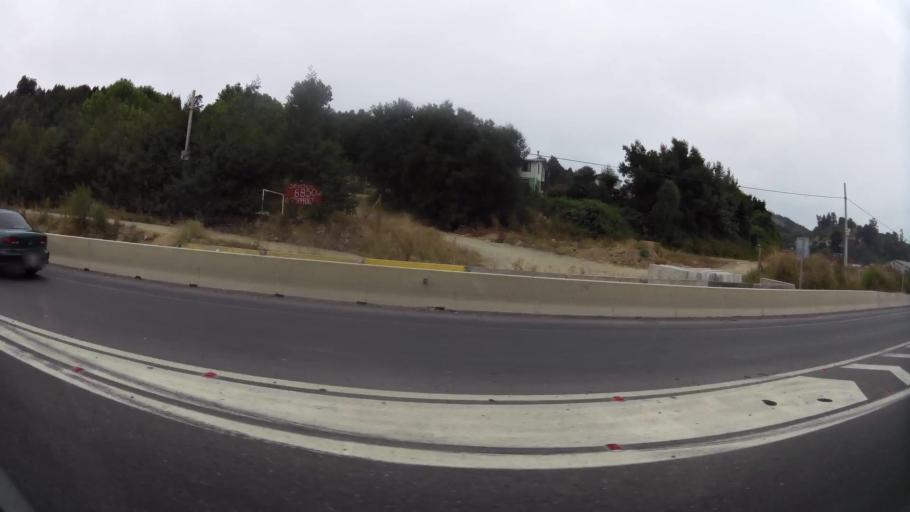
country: CL
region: Biobio
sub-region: Provincia de Concepcion
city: Concepcion
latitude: -36.8160
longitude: -72.9860
